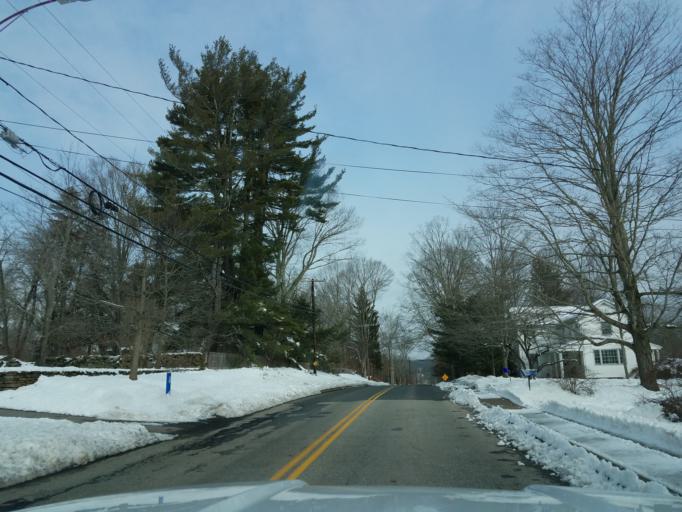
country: US
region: Connecticut
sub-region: Middlesex County
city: Lake Pocotopaug
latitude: 41.5872
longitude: -72.5078
